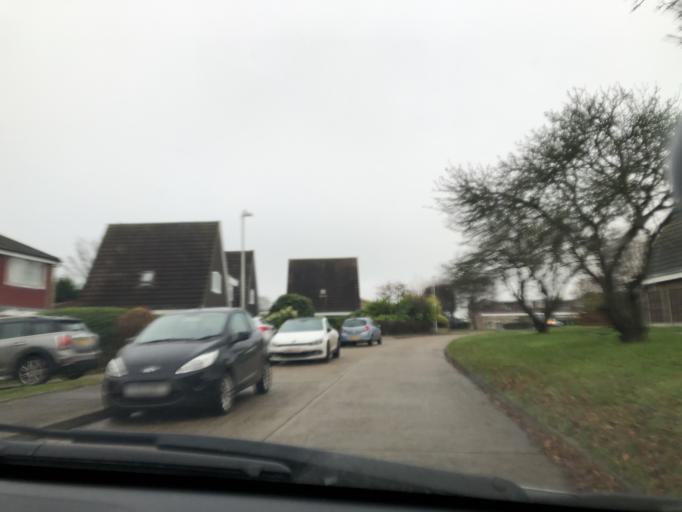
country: GB
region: England
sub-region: Kent
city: Meopham
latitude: 51.4073
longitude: 0.3517
